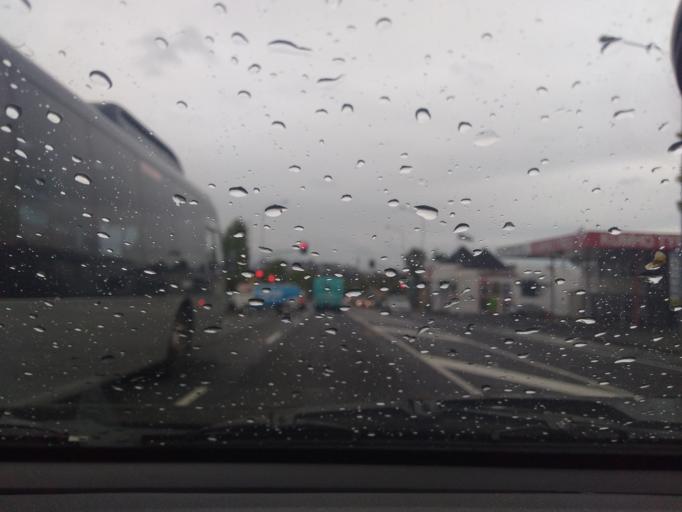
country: NZ
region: Auckland
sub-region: Auckland
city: Rosebank
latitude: -36.8700
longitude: 174.7115
